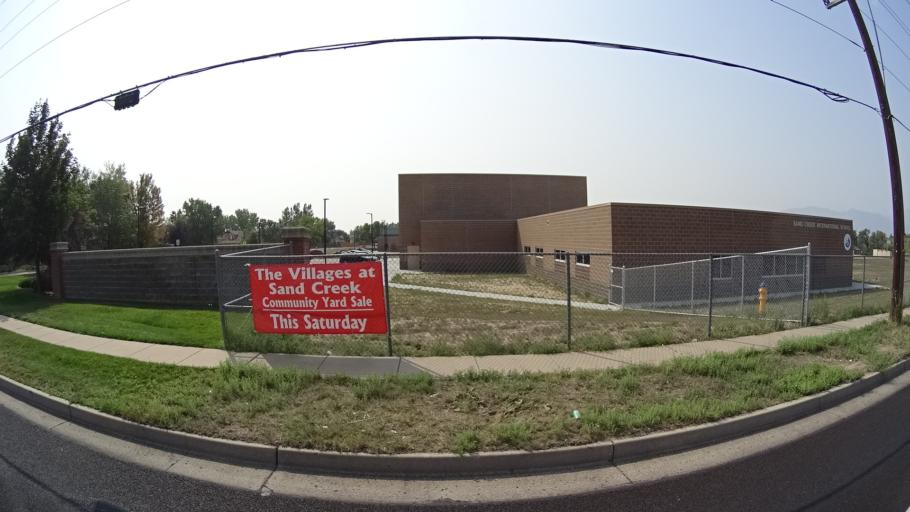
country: US
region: Colorado
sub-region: El Paso County
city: Cimarron Hills
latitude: 38.8253
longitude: -104.7397
